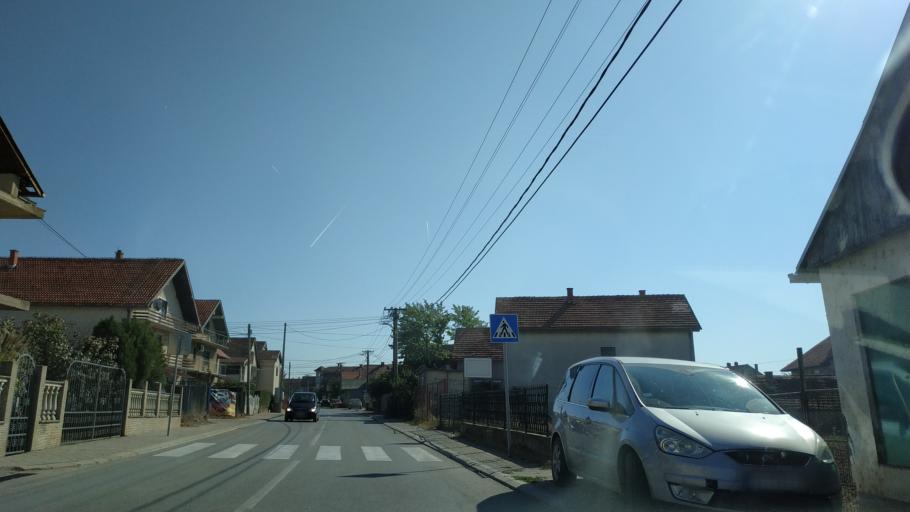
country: RS
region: Central Serbia
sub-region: Nisavski Okrug
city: Aleksinac
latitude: 43.5430
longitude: 21.6923
